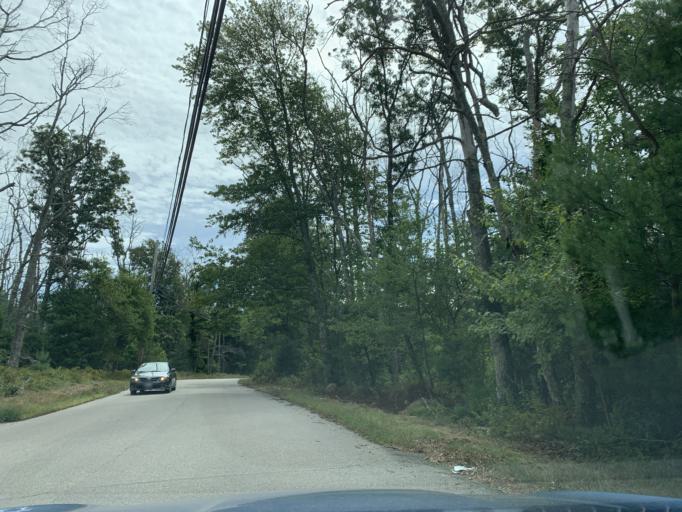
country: US
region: Rhode Island
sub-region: Washington County
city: Exeter
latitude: 41.5493
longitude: -71.6185
